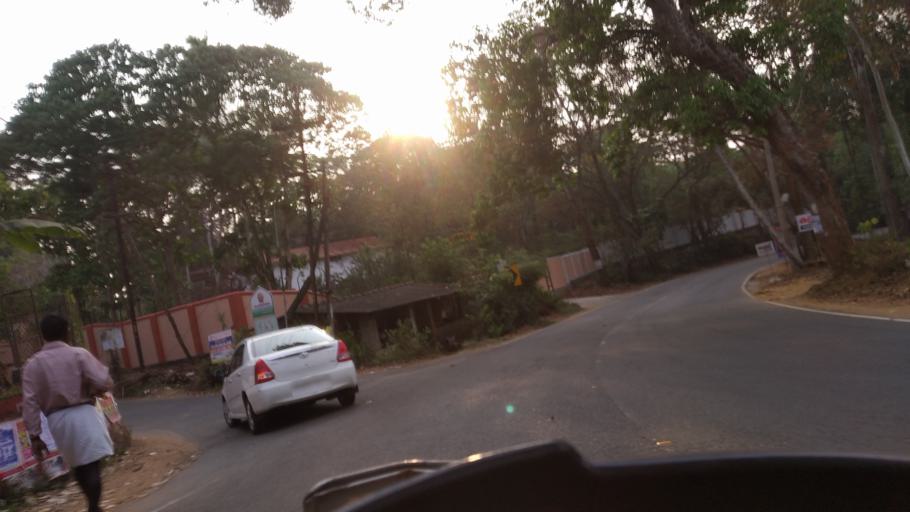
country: IN
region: Kerala
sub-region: Kottayam
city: Lalam
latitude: 9.5630
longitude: 76.6998
